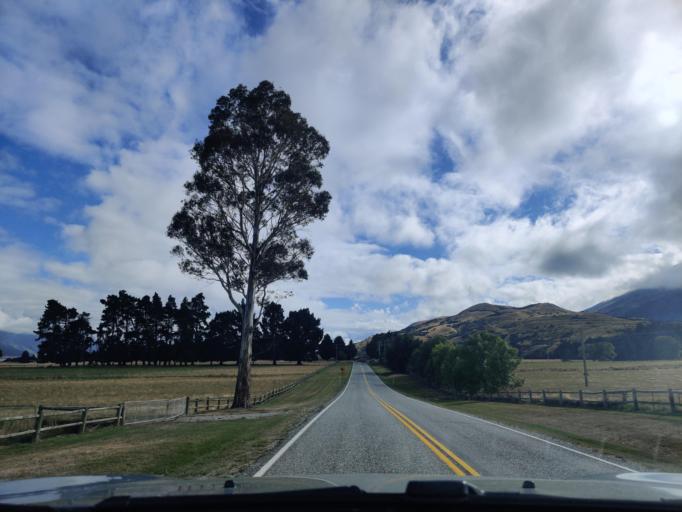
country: NZ
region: Otago
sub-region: Queenstown-Lakes District
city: Queenstown
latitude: -44.8666
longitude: 168.4031
